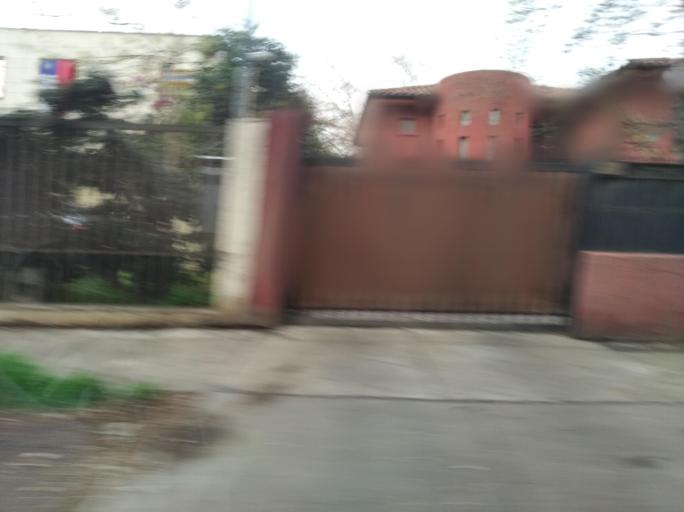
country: CL
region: Santiago Metropolitan
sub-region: Provincia de Santiago
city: Villa Presidente Frei, Nunoa, Santiago, Chile
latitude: -33.4883
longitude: -70.5979
